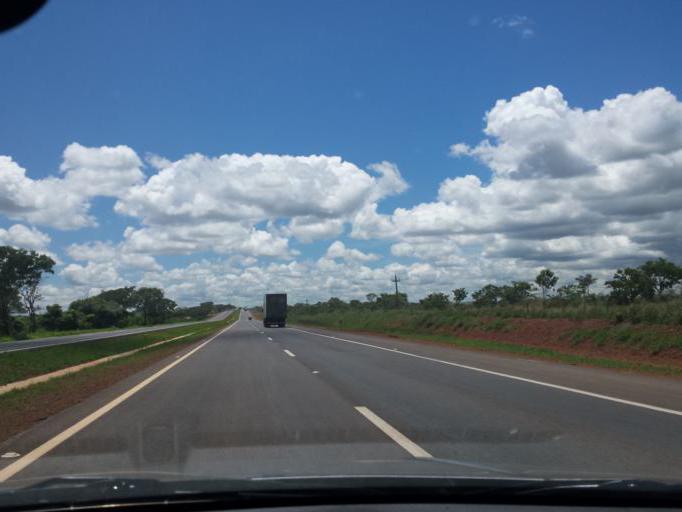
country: BR
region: Goias
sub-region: Cristalina
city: Cristalina
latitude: -16.6867
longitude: -47.7016
